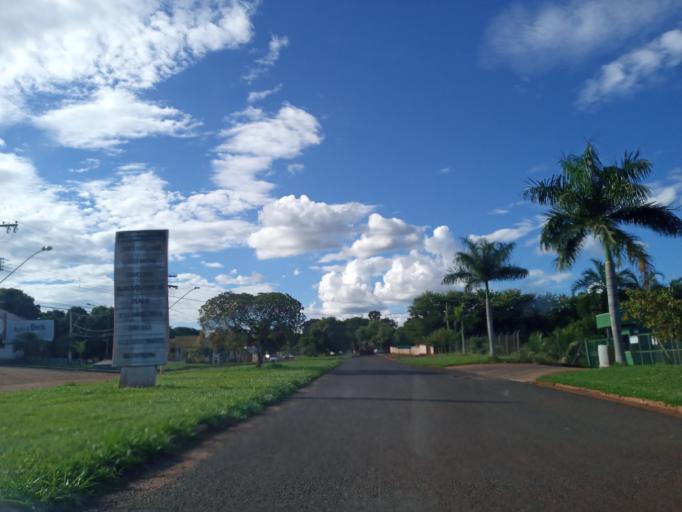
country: BR
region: Minas Gerais
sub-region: Ituiutaba
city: Ituiutaba
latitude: -18.9654
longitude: -49.4905
